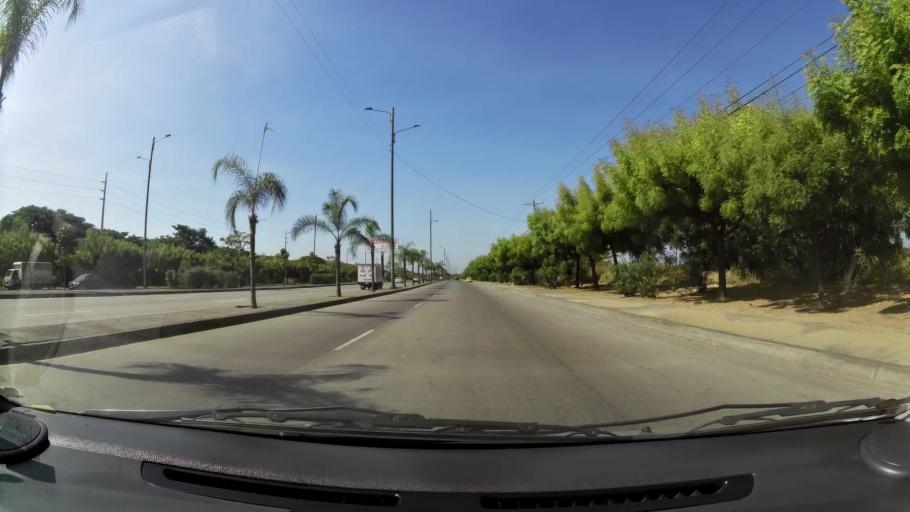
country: EC
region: Guayas
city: Eloy Alfaro
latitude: -2.1074
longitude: -79.8873
